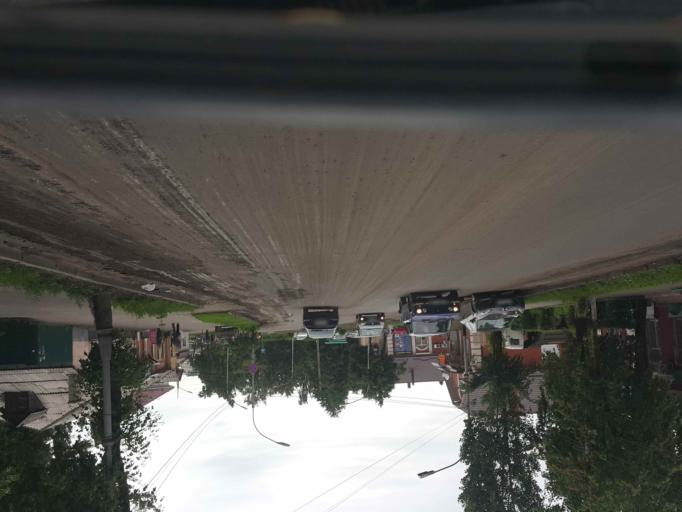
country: RU
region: Tambov
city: Michurinsk
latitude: 52.8953
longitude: 40.4985
